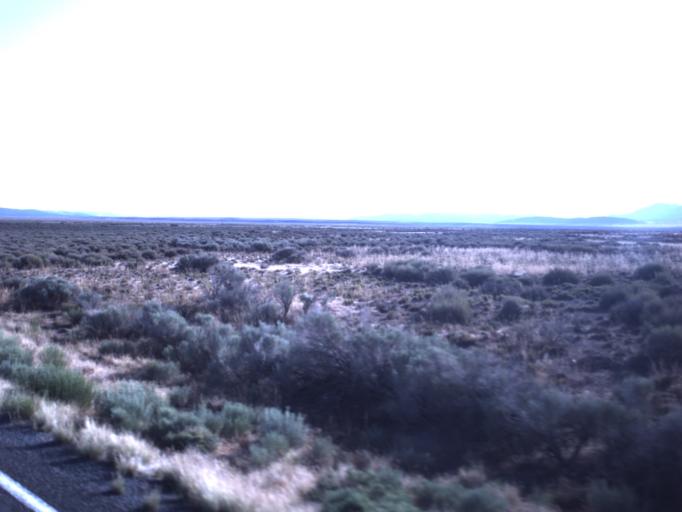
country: US
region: Utah
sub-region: Iron County
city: Enoch
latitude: 37.9074
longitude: -113.0315
